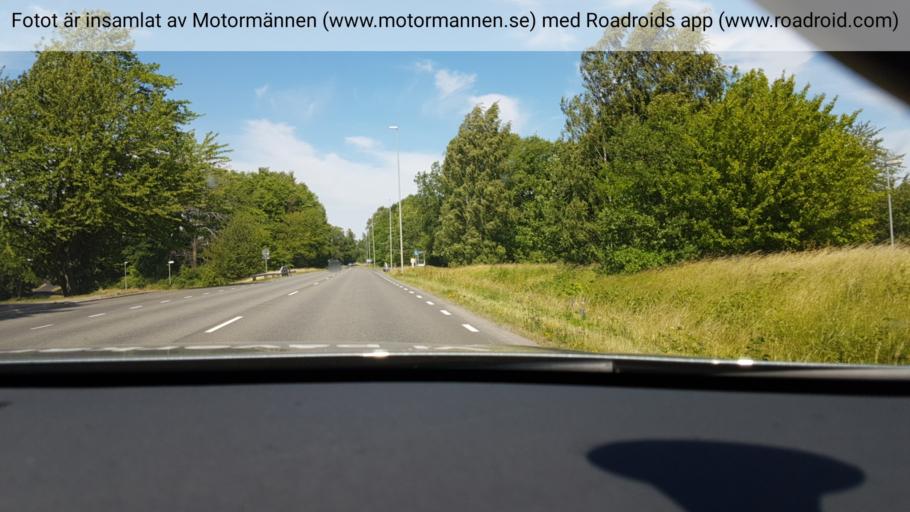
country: SE
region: Vaestra Goetaland
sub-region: Skovde Kommun
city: Skoevde
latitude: 58.4185
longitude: 13.8444
